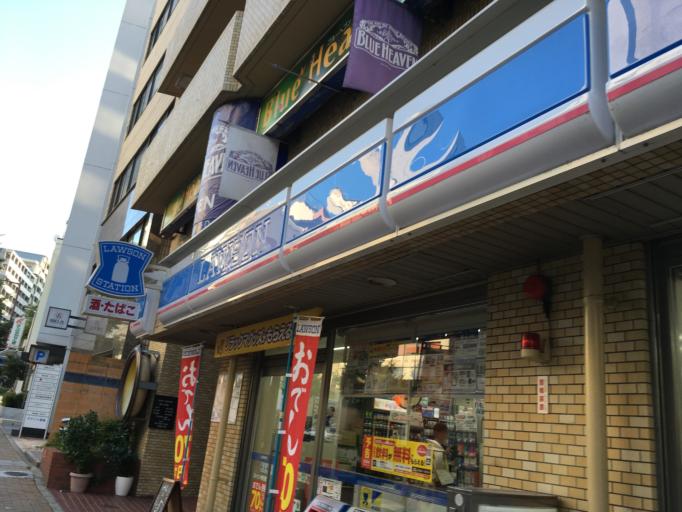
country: JP
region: Hyogo
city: Kobe
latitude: 34.6994
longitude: 135.1939
